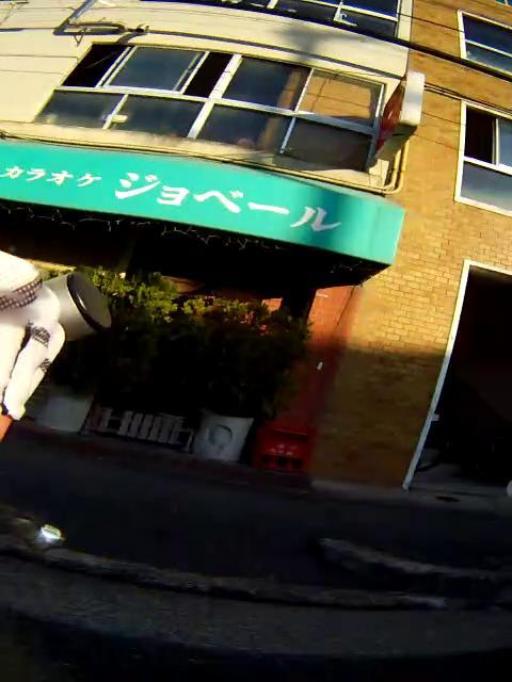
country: JP
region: Hyogo
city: Itami
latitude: 34.7618
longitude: 135.4118
